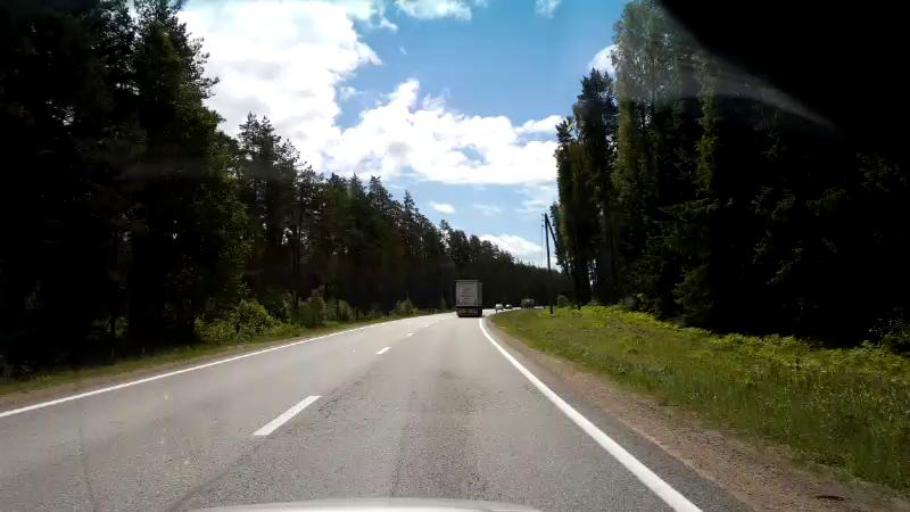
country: LV
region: Salacgrivas
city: Salacgriva
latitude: 57.5721
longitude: 24.4344
